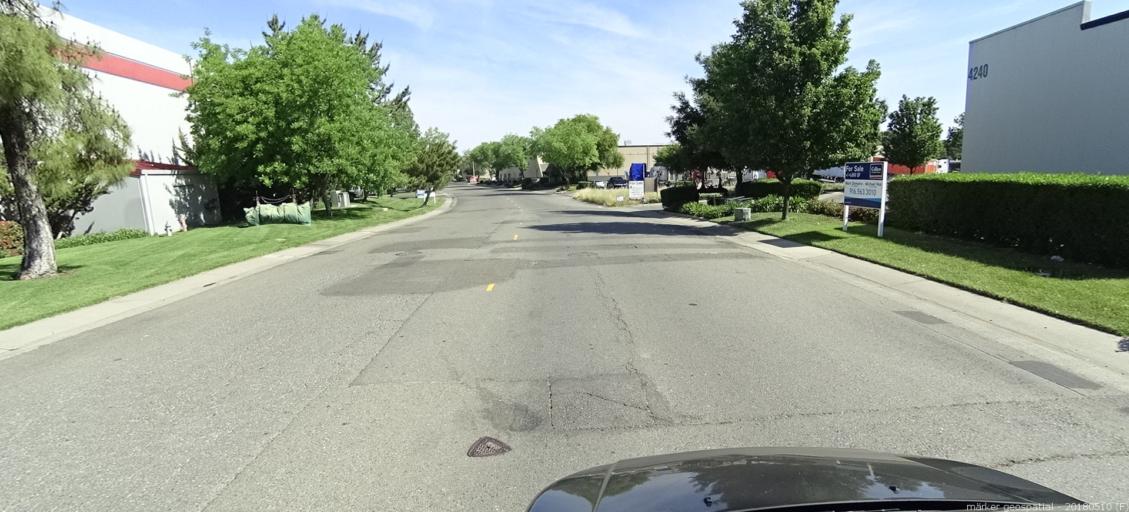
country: US
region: California
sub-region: Sacramento County
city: Rio Linda
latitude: 38.6457
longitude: -121.4701
